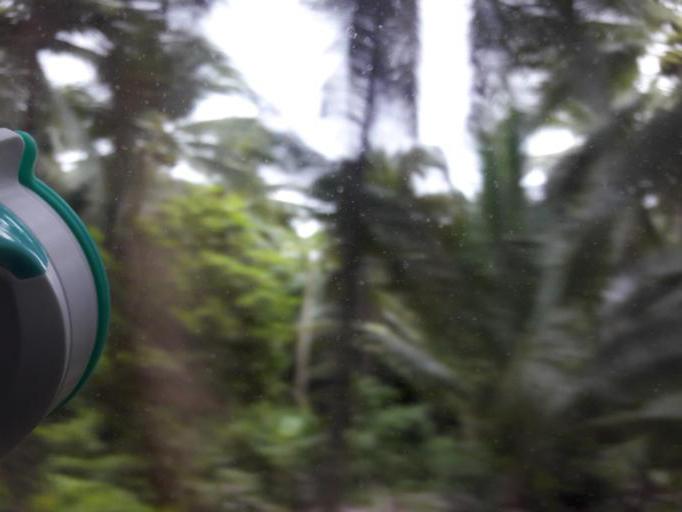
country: TH
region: Ratchaburi
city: Damnoen Saduak
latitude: 13.5364
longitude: 100.0081
